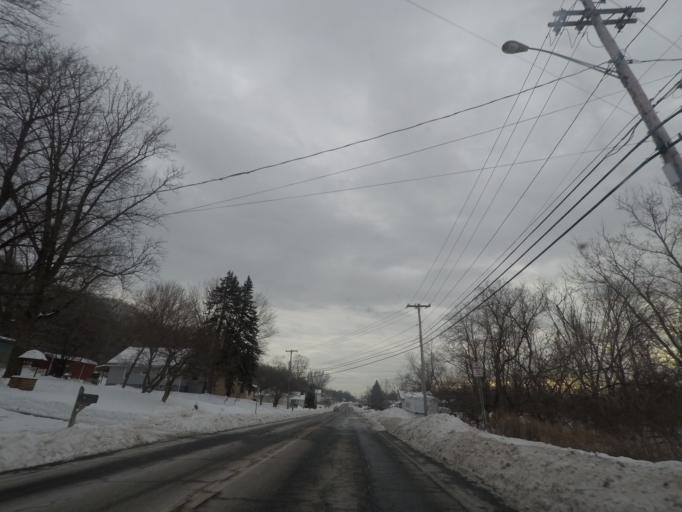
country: US
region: New York
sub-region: Rensselaer County
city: Hampton Manor
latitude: 42.6253
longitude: -73.7446
